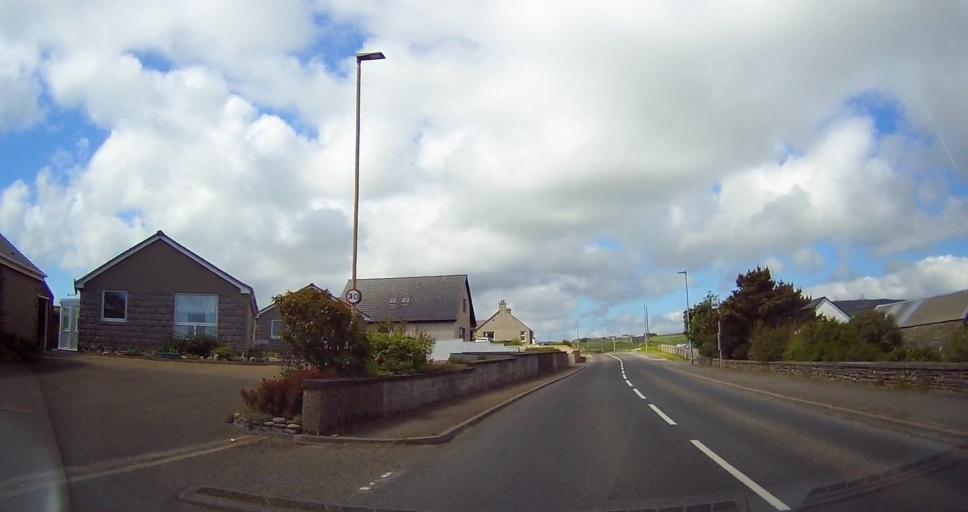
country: GB
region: Scotland
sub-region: Orkney Islands
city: Orkney
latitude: 58.9775
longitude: -2.9819
